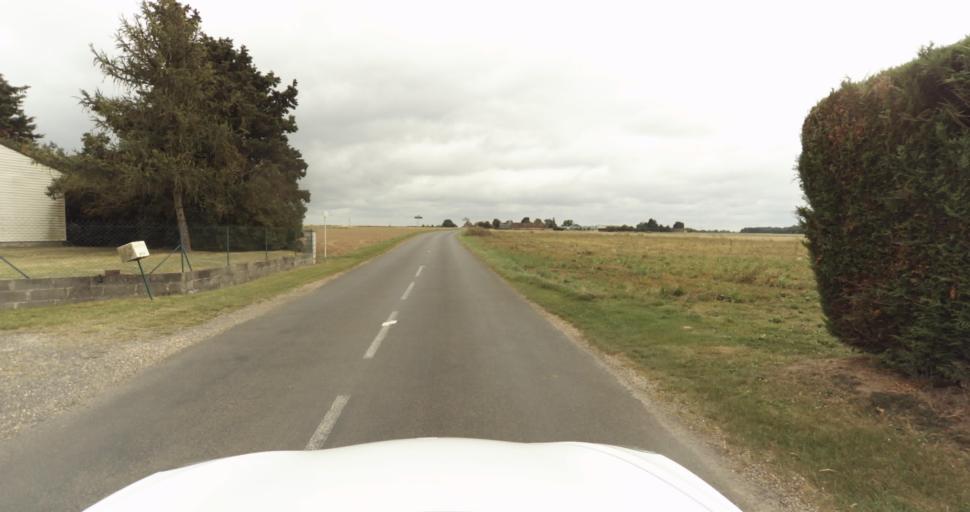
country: FR
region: Haute-Normandie
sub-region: Departement de l'Eure
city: Damville
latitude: 48.9342
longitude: 1.0811
